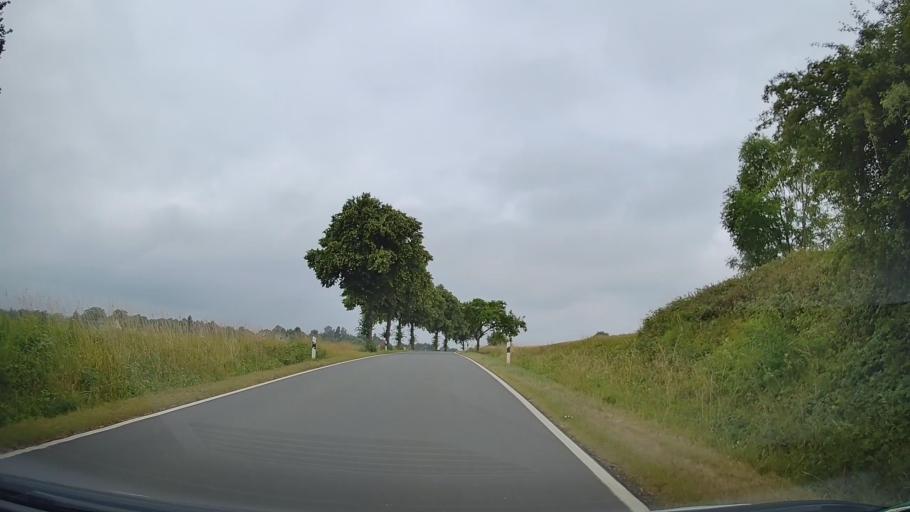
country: DE
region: Lower Saxony
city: Rinteln
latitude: 52.1577
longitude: 9.0933
